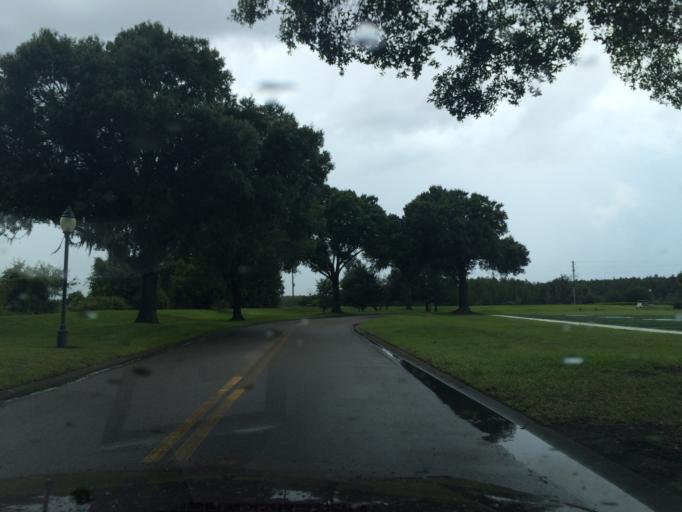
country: US
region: Florida
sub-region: Pasco County
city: Wesley Chapel
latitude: 28.2261
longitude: -82.3353
